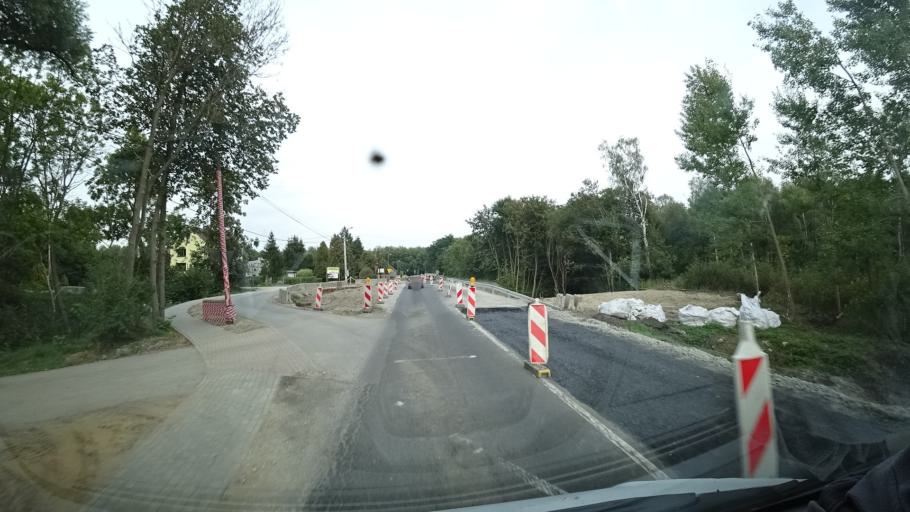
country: PL
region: Silesian Voivodeship
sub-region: Powiat gliwicki
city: Pyskowice
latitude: 50.3922
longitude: 18.5981
